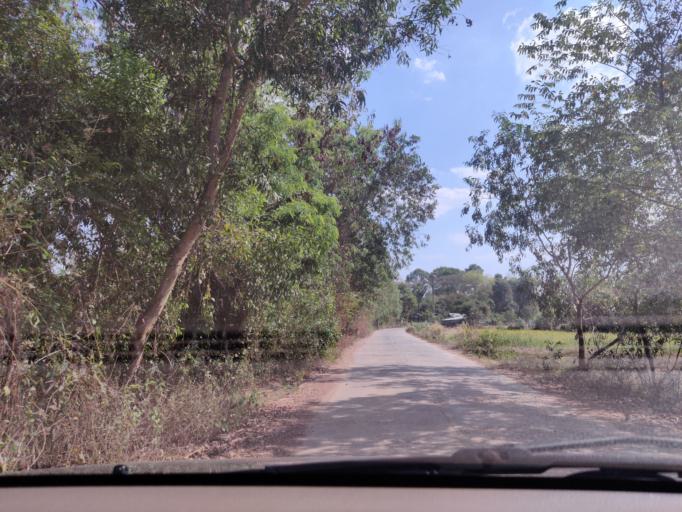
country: TH
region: Sisaket
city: Si Sa Ket
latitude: 15.0682
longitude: 104.3497
